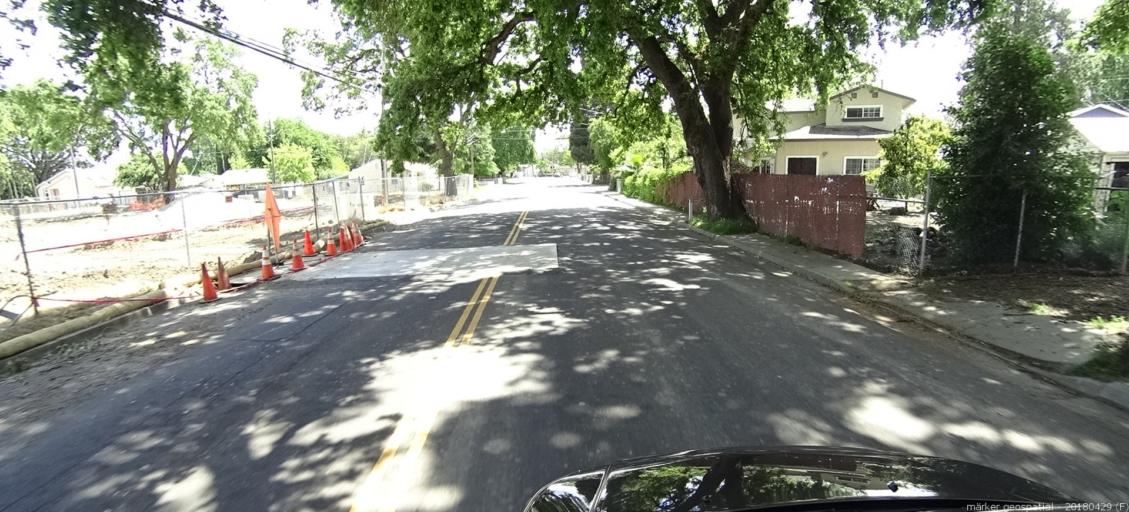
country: US
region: California
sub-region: Yolo County
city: West Sacramento
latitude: 38.5923
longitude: -121.5375
